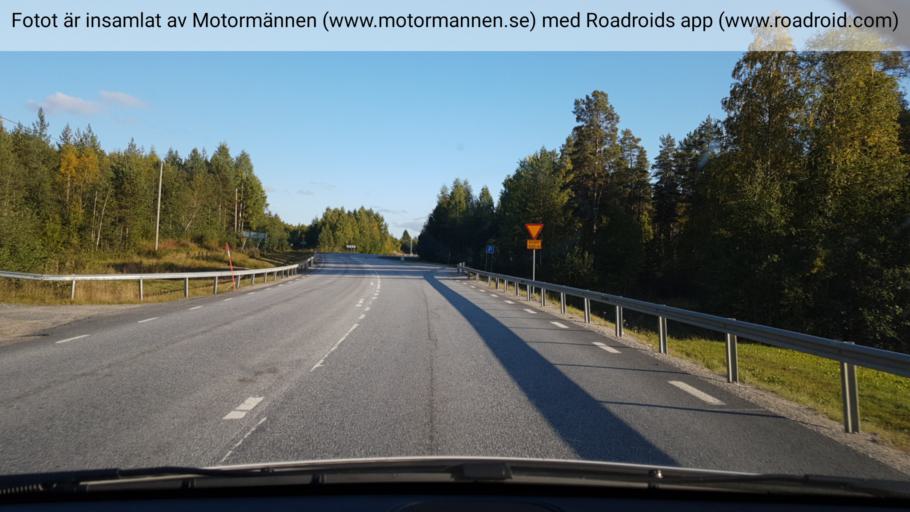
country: SE
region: Vaesterbotten
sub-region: Vannas Kommun
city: Vaennaes
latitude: 63.9247
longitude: 19.7781
